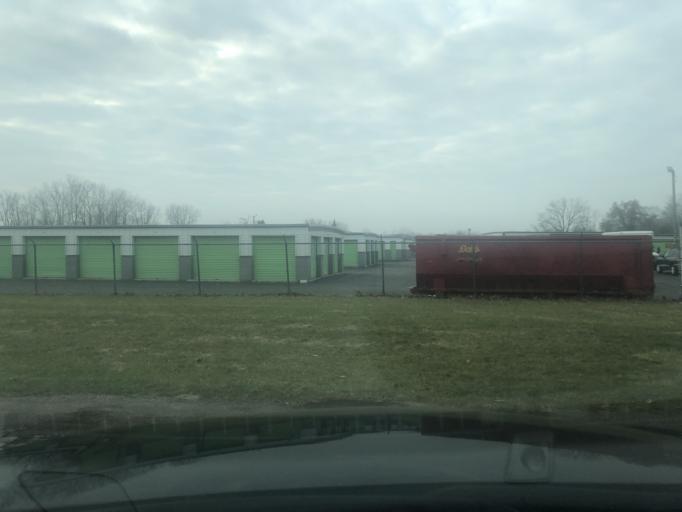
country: US
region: Michigan
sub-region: Wayne County
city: Belleville
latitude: 42.2217
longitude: -83.5413
